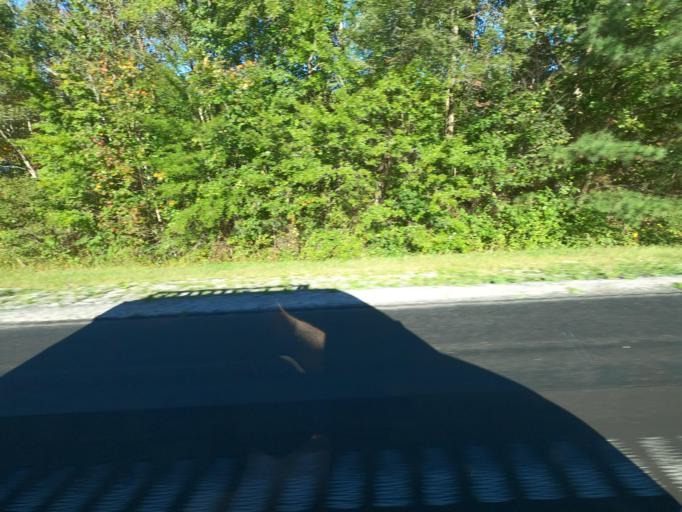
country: US
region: Tennessee
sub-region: Coffee County
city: Manchester
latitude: 35.4287
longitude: -86.0283
